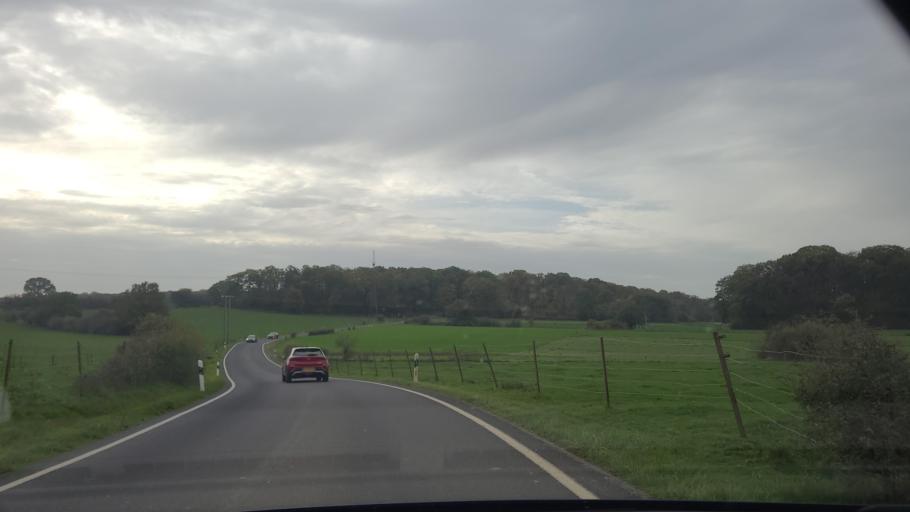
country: LU
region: Luxembourg
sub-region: Canton de Capellen
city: Mamer
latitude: 49.6209
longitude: 6.0210
